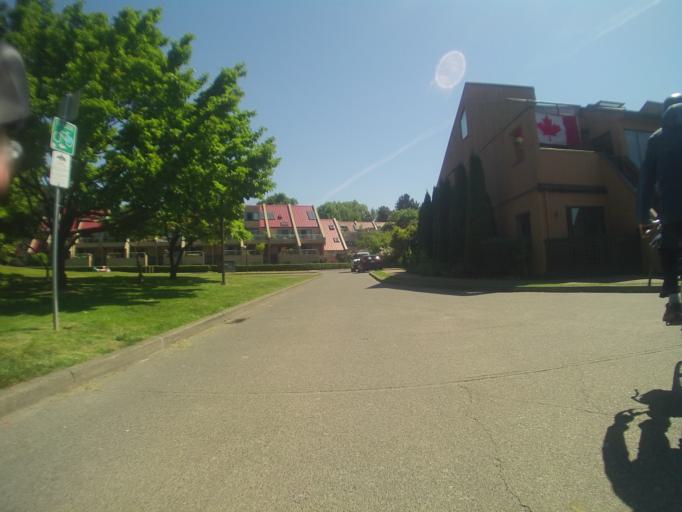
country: CA
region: British Columbia
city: West End
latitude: 49.2680
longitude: -123.1277
